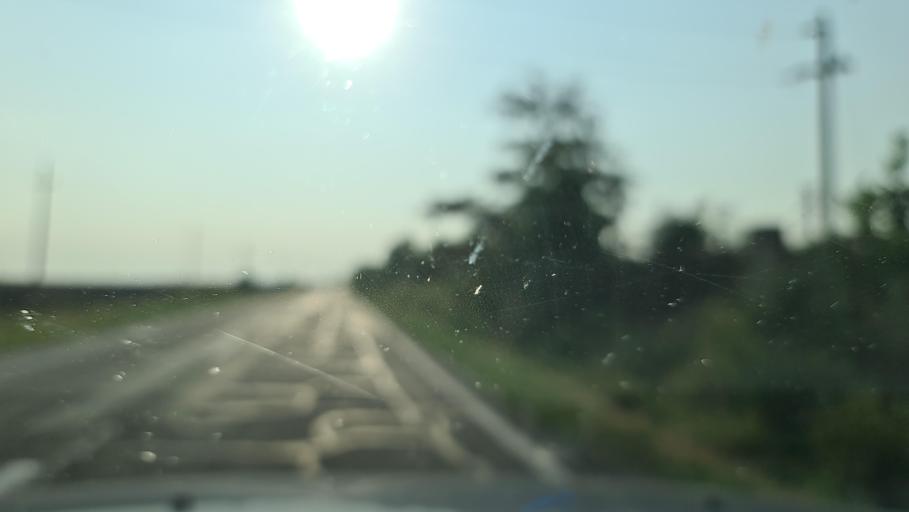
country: RO
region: Calarasi
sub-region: Comuna Dor Marunt
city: Dor Marunt
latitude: 44.4364
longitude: 26.9657
